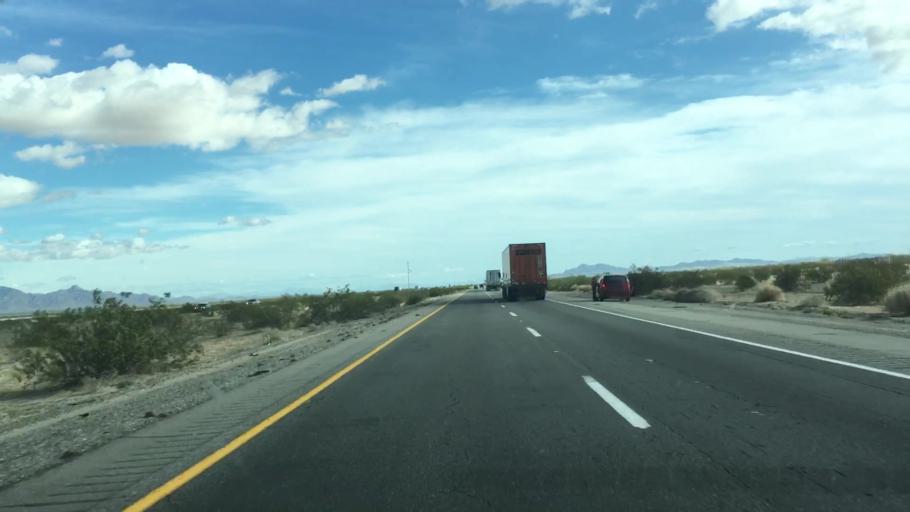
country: US
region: California
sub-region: Riverside County
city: Mesa Verde
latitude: 33.6288
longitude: -115.0676
